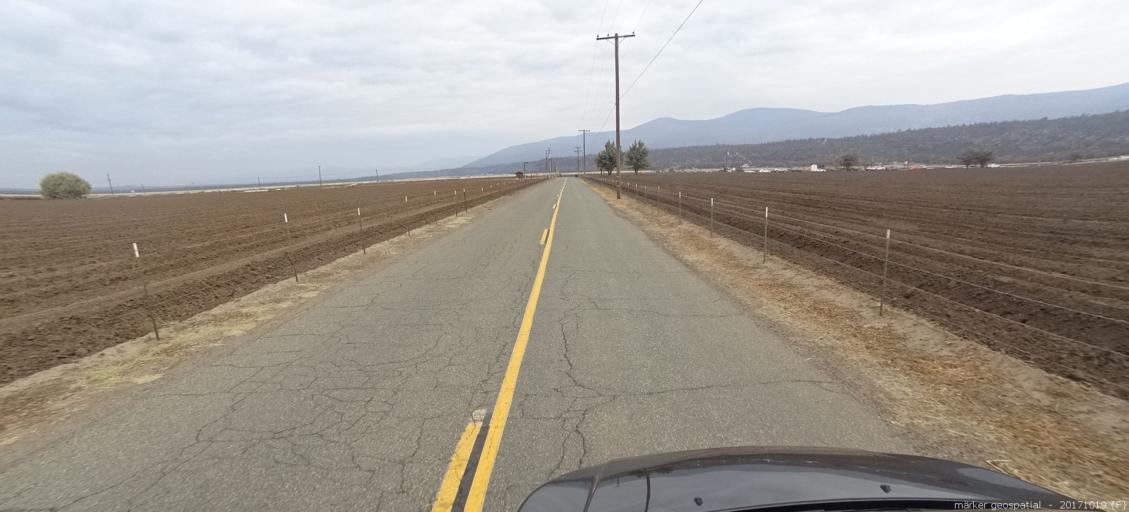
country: US
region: California
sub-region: Shasta County
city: Burney
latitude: 41.0786
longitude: -121.3314
